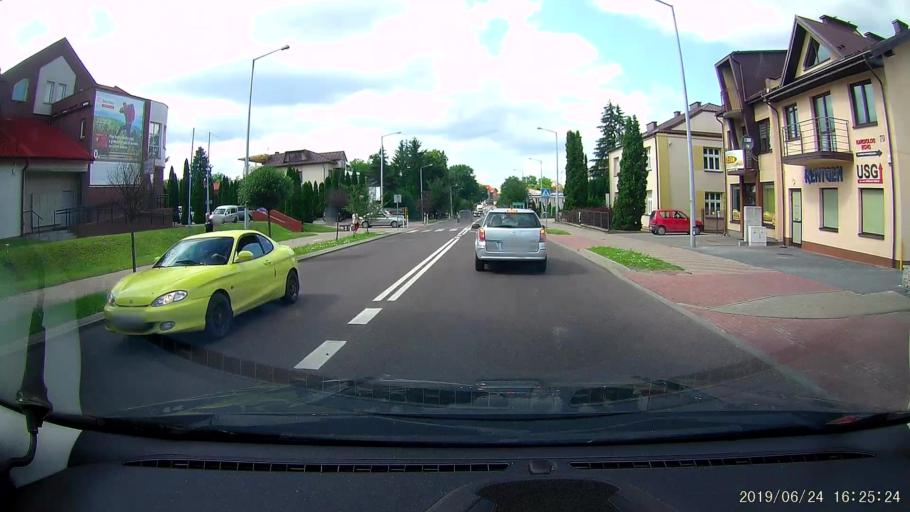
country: PL
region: Lublin Voivodeship
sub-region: Powiat tomaszowski
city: Tomaszow Lubelski
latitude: 50.4438
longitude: 23.4174
